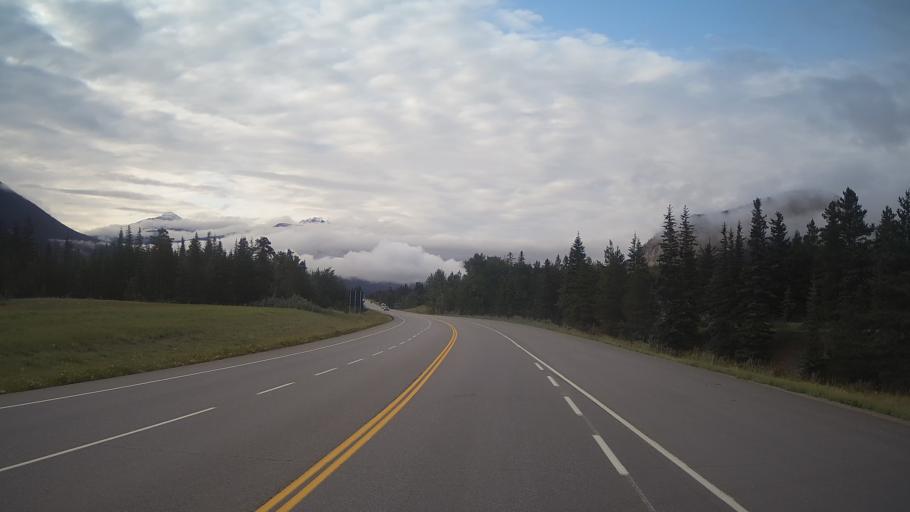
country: CA
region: Alberta
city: Jasper Park Lodge
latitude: 52.9702
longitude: -118.0569
